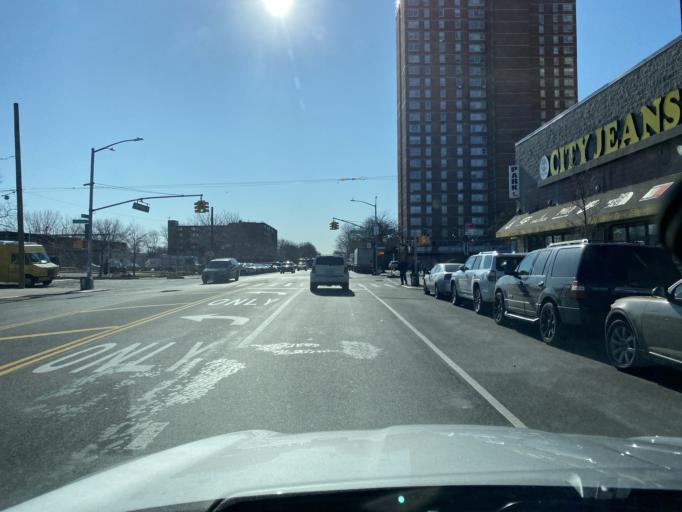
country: US
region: New York
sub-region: Bronx
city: The Bronx
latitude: 40.8225
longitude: -73.8584
